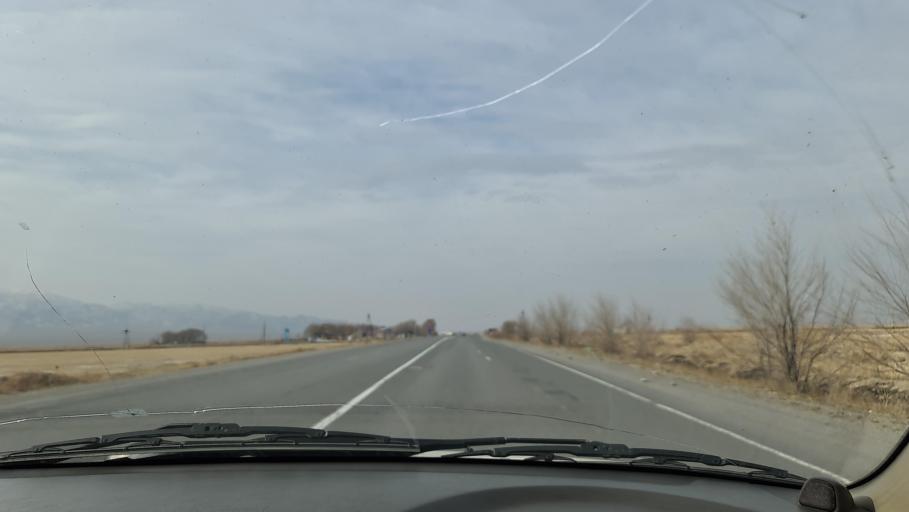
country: KG
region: Chuy
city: Tokmok
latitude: 43.3494
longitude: 75.4833
